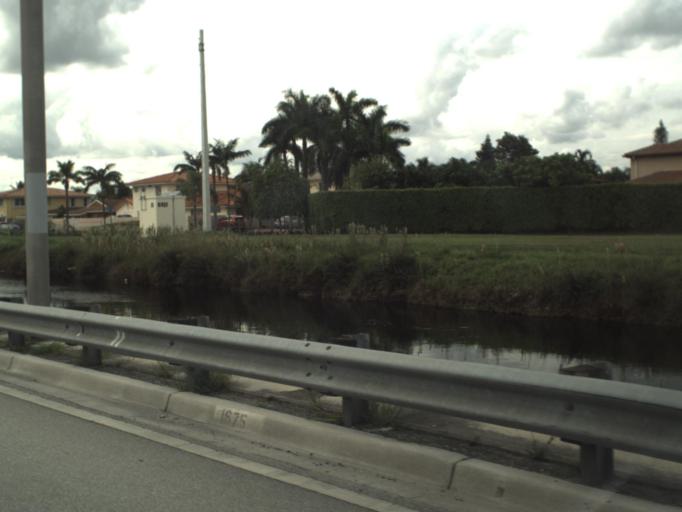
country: US
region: Florida
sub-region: Miami-Dade County
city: Tamiami
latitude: 25.7612
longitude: -80.3880
